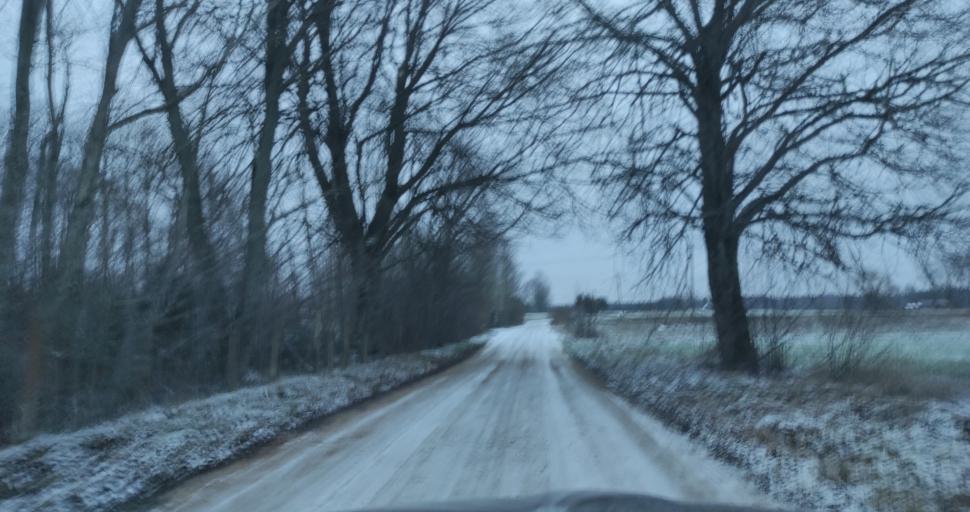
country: LV
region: Kuldigas Rajons
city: Kuldiga
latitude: 56.9699
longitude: 22.0619
